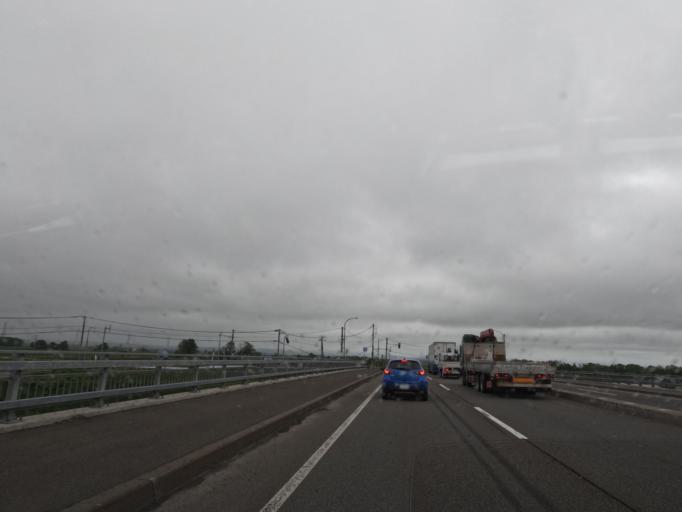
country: JP
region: Hokkaido
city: Tobetsu
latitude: 43.1631
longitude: 141.5198
